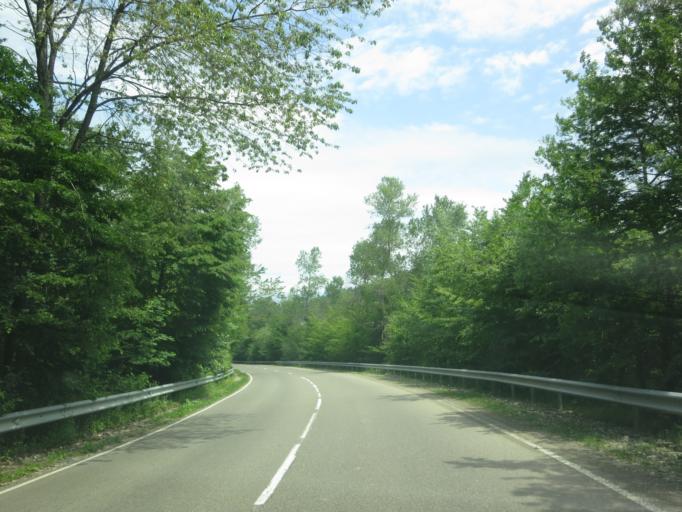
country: GE
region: Kakheti
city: Sagarejo
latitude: 41.8645
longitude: 45.3519
